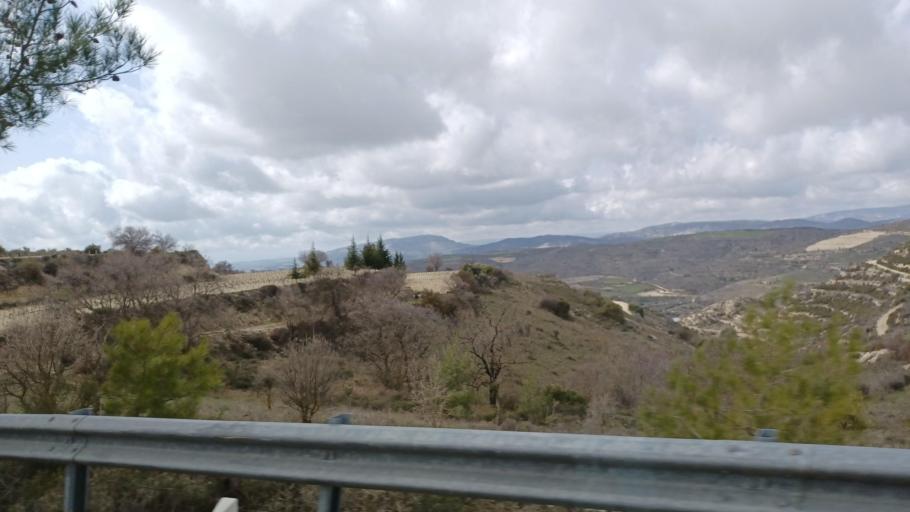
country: CY
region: Limassol
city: Pachna
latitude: 34.8277
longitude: 32.7698
